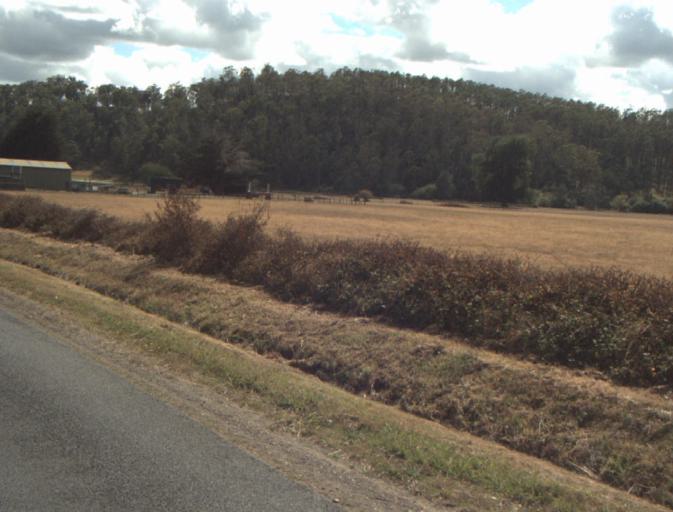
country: AU
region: Tasmania
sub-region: Launceston
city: Mayfield
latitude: -41.2521
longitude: 147.1474
